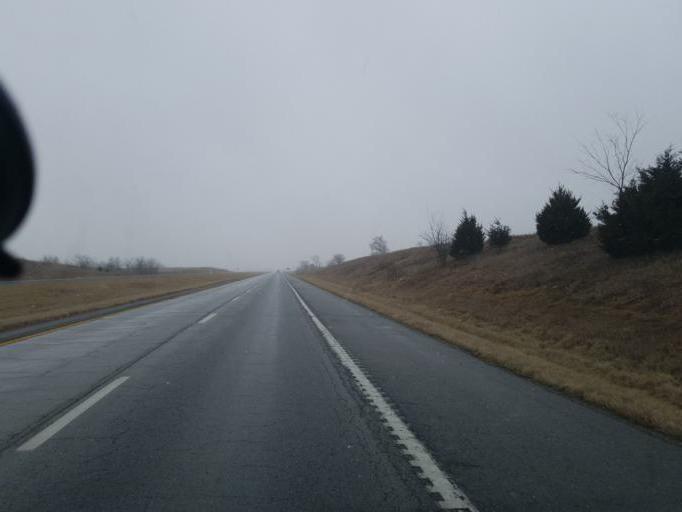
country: US
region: Missouri
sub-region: Macon County
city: La Plata
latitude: 39.9907
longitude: -92.4758
